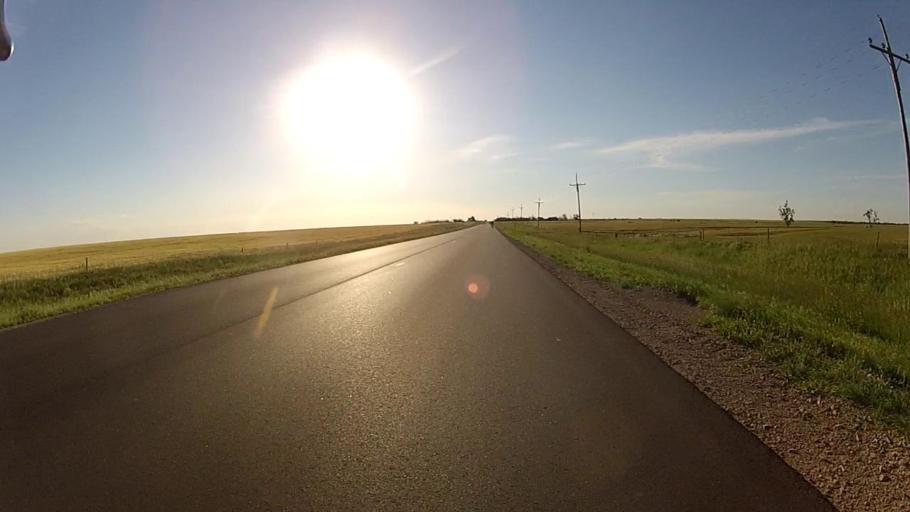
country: US
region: Kansas
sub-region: Comanche County
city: Coldwater
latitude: 37.2817
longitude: -99.1596
